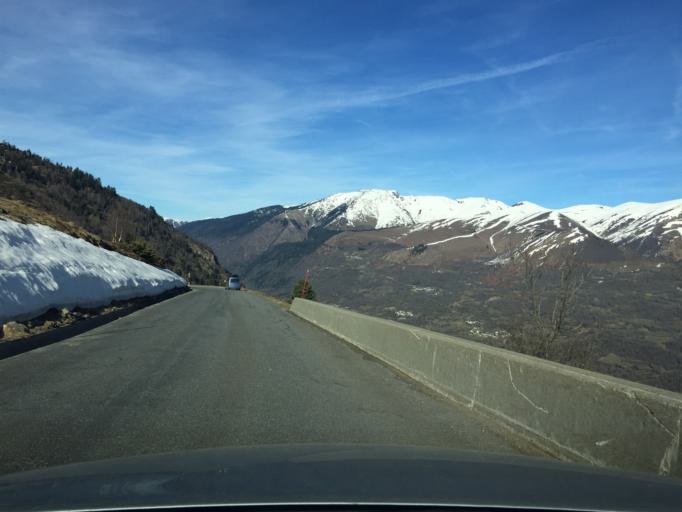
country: FR
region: Midi-Pyrenees
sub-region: Departement des Hautes-Pyrenees
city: Saint-Lary-Soulan
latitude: 42.7988
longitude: 0.3899
